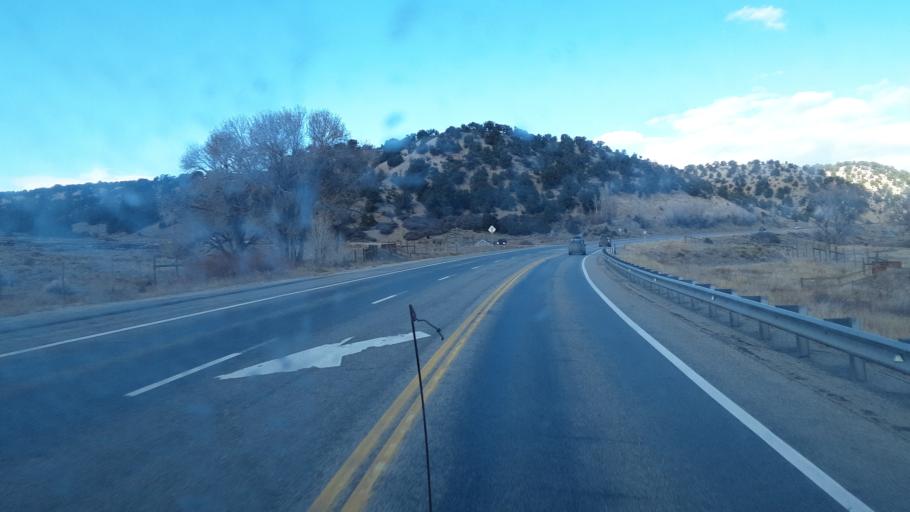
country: US
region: Colorado
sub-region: Chaffee County
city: Buena Vista
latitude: 38.7816
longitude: -106.1124
